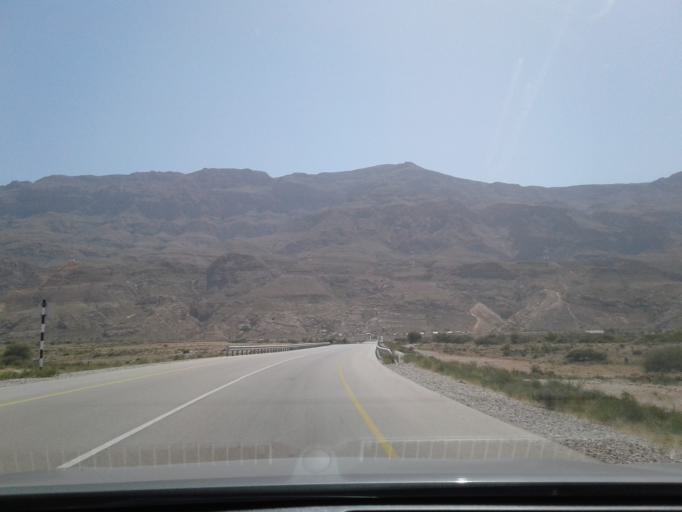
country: OM
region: Ash Sharqiyah
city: Al Qabil
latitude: 23.0310
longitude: 59.0822
